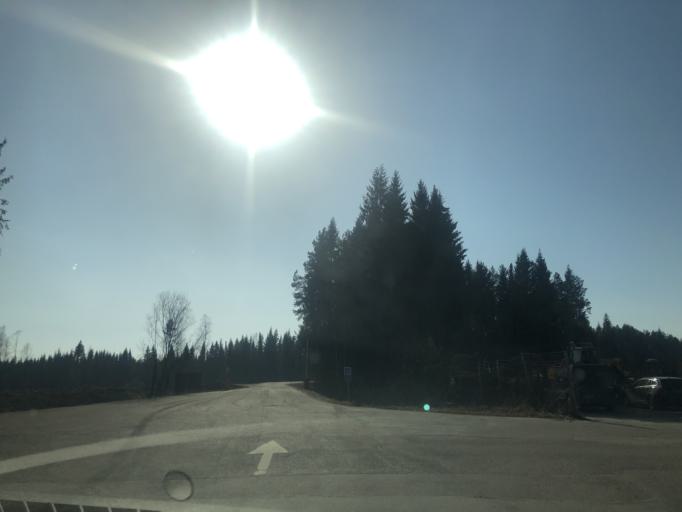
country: SE
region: Vaermland
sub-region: Filipstads Kommun
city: Filipstad
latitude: 59.7863
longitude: 14.2678
